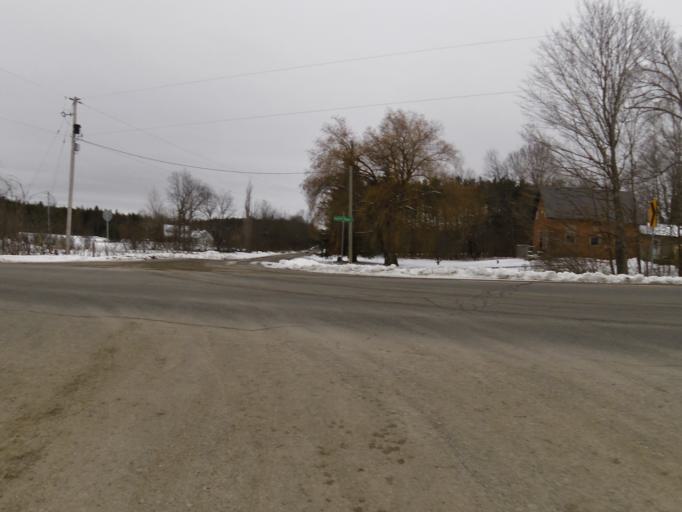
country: CA
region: Ontario
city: Carleton Place
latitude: 45.1243
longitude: -76.2471
